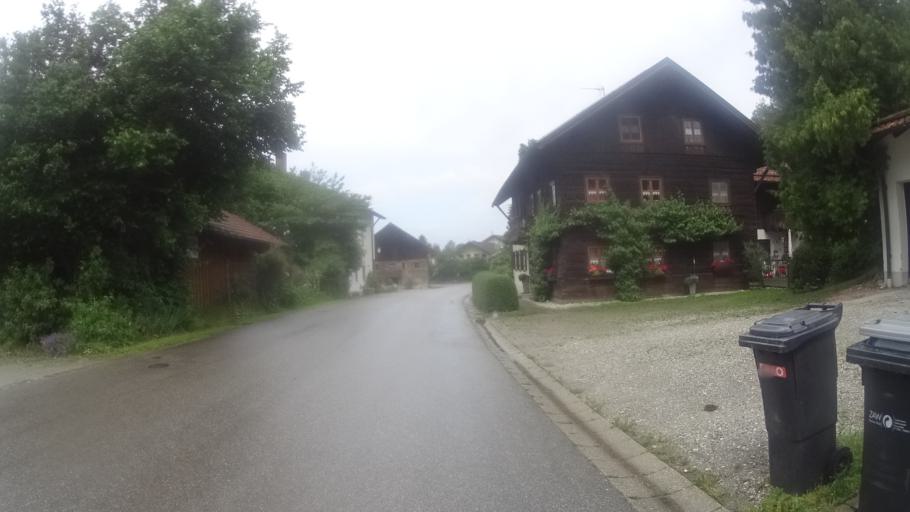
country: DE
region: Bavaria
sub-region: Lower Bavaria
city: Bad Griesbach
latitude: 48.4203
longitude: 13.1844
